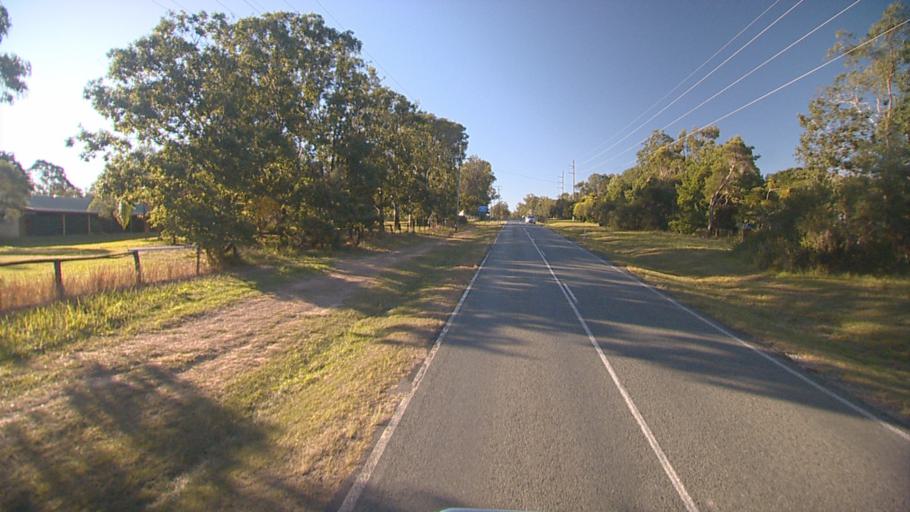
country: AU
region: Queensland
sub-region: Logan
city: Logan Reserve
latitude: -27.7375
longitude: 153.0875
